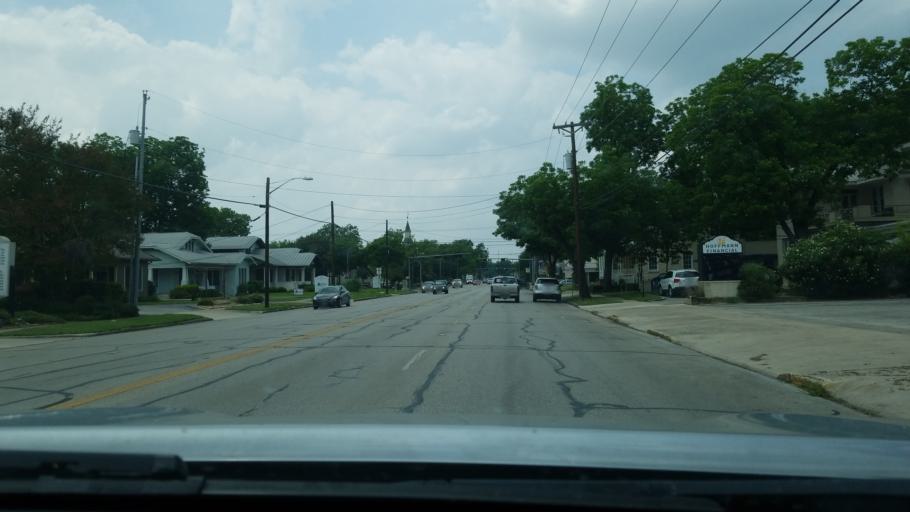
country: US
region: Texas
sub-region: Comal County
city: New Braunfels
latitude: 29.6996
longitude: -98.1196
